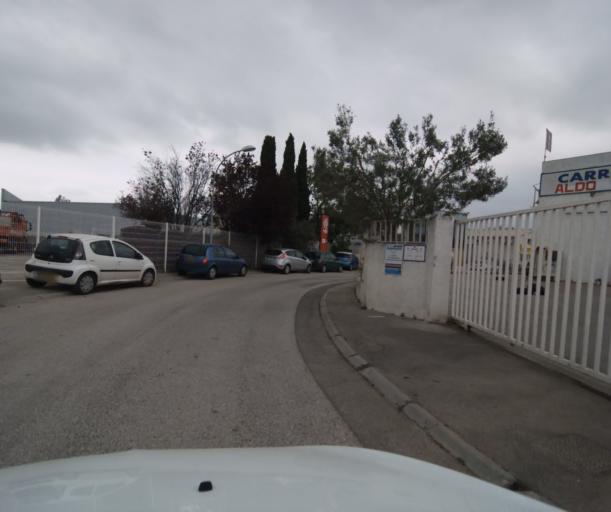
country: FR
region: Provence-Alpes-Cote d'Azur
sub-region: Departement du Var
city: La Crau
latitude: 43.1326
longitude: 6.0712
